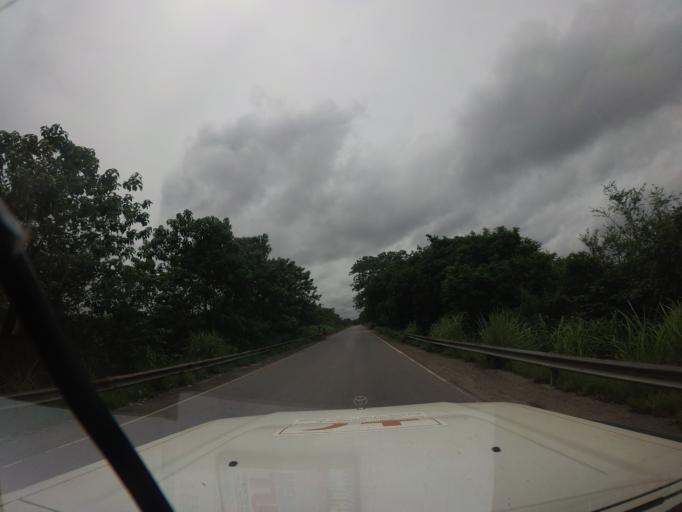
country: SL
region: Northern Province
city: Magburaka
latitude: 8.7444
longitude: -11.9624
